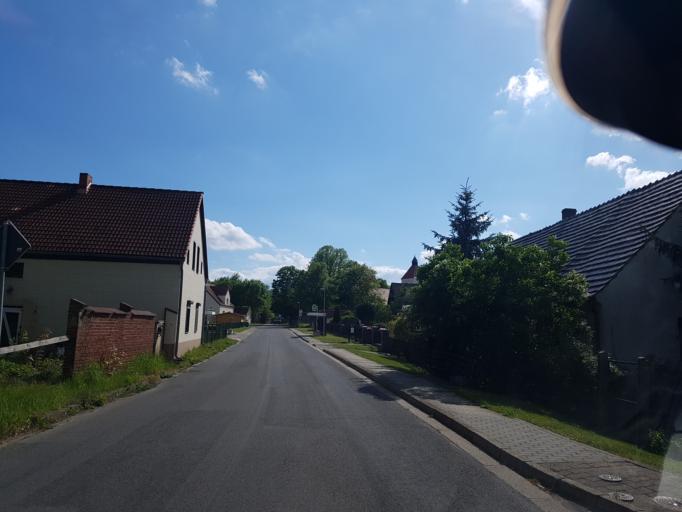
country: DE
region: Brandenburg
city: Cottbus
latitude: 51.6684
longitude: 14.3467
